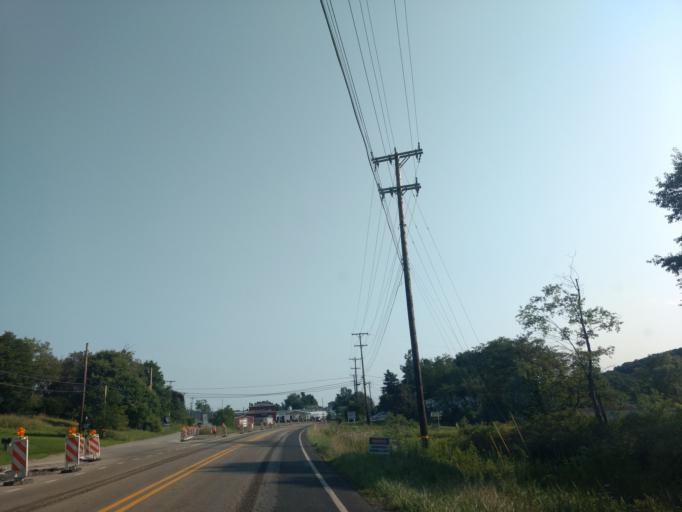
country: US
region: Pennsylvania
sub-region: Butler County
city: Zelienople
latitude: 40.8163
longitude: -80.1239
